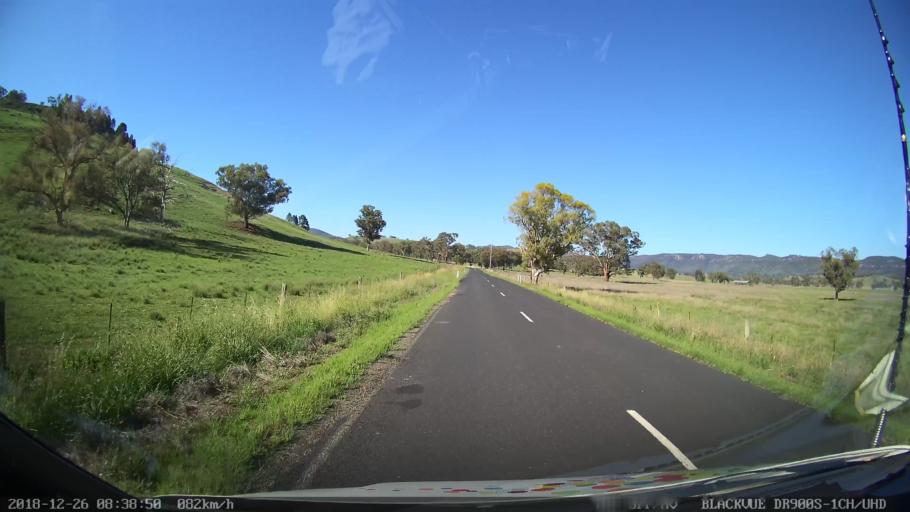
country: AU
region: New South Wales
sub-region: Upper Hunter Shire
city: Merriwa
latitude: -32.4470
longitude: 150.0791
